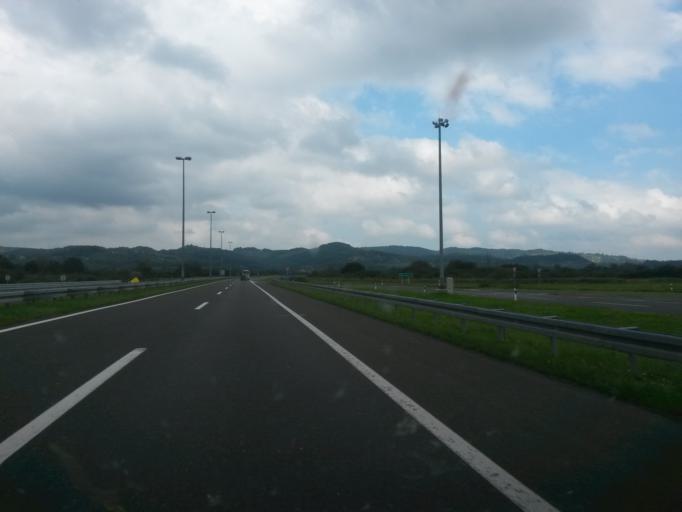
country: HR
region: Varazdinska
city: Ljubescica
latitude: 46.1704
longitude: 16.3750
